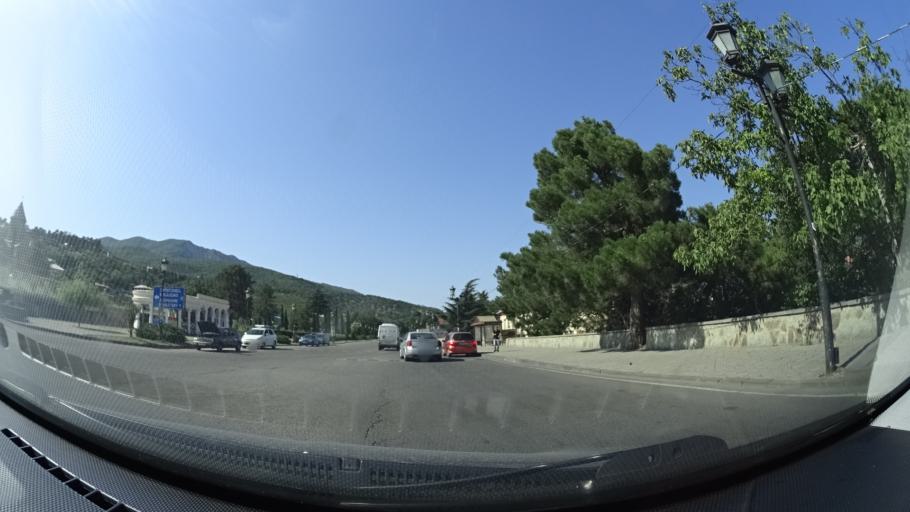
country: GE
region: Mtskheta-Mtianeti
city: Mtskheta
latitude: 41.8456
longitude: 44.7205
